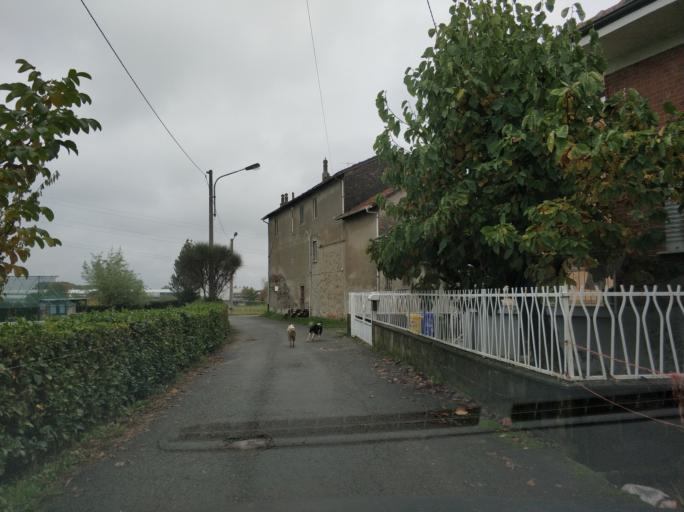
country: IT
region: Piedmont
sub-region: Provincia di Torino
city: Mathi
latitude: 45.2493
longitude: 7.5461
